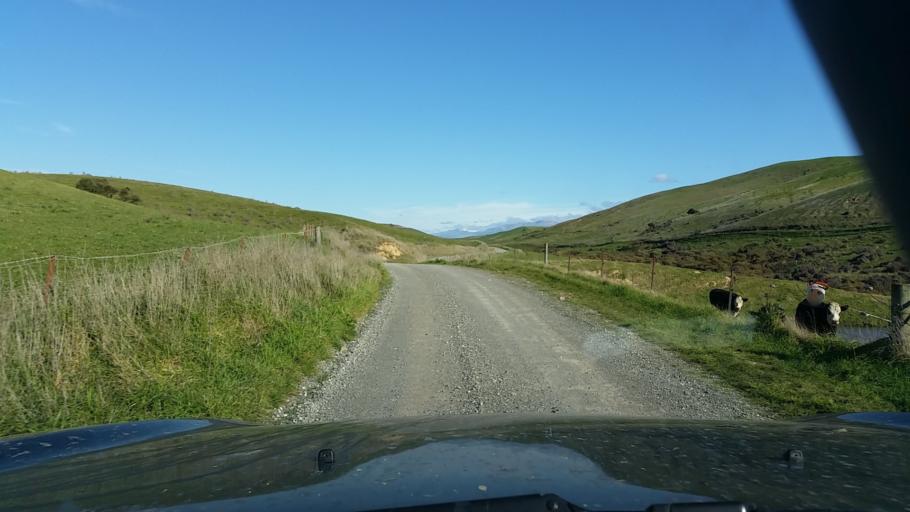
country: NZ
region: Marlborough
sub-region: Marlborough District
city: Blenheim
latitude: -41.6689
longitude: 174.1354
